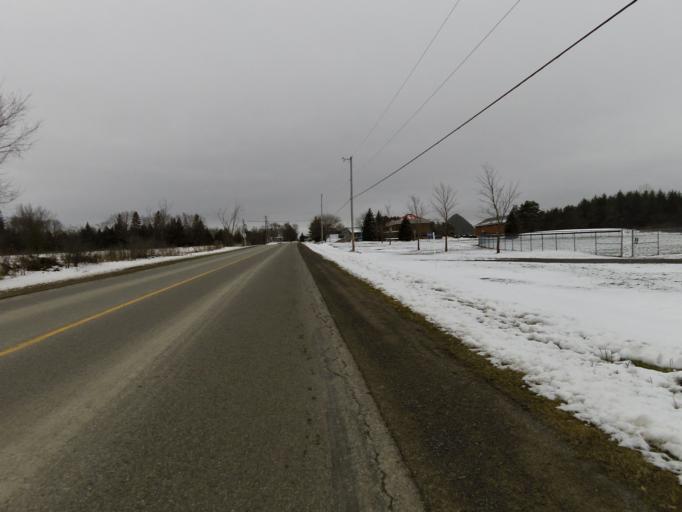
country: CA
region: Ontario
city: Carleton Place
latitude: 45.2100
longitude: -76.2090
